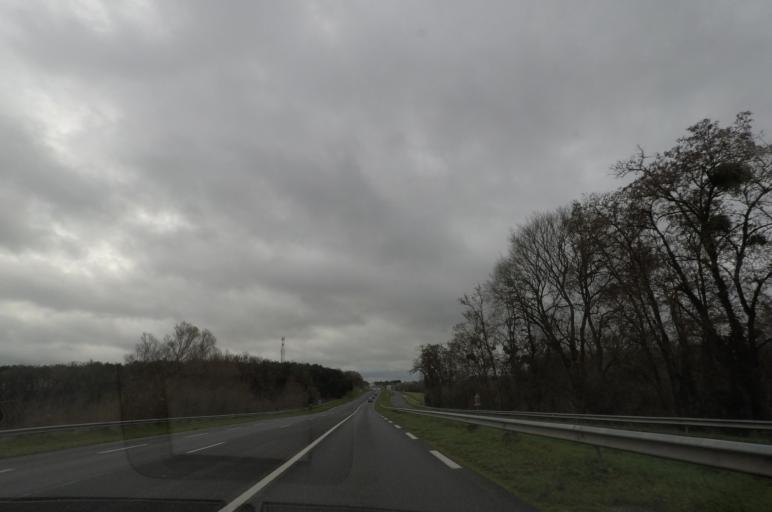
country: FR
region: Centre
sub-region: Departement du Loir-et-Cher
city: Saint-Sulpice-de-Pommeray
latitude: 47.6542
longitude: 1.2715
